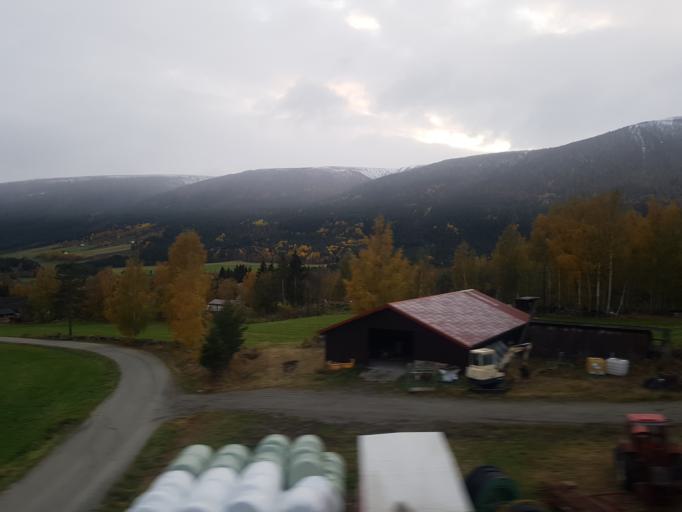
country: NO
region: Oppland
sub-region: Dovre
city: Dovre
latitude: 61.9670
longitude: 9.2614
